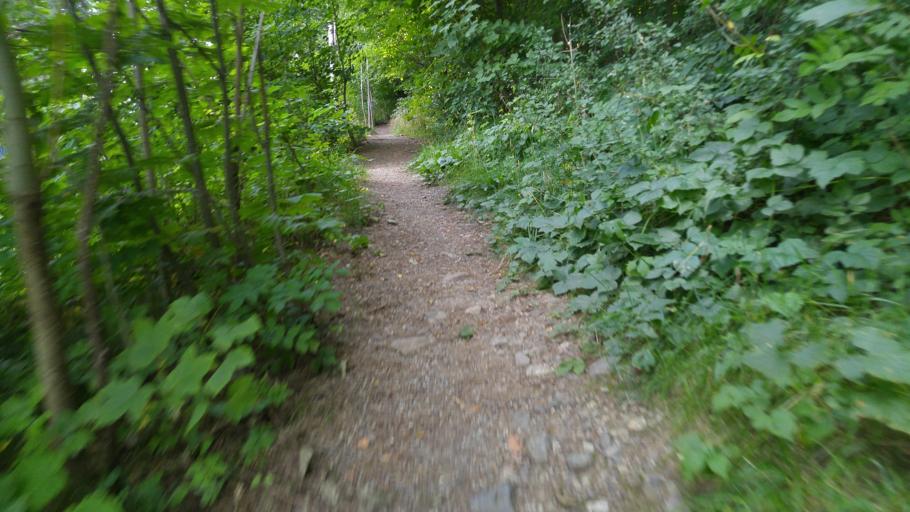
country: NO
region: Akershus
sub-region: Asker
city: Billingstad
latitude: 59.8440
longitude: 10.4894
